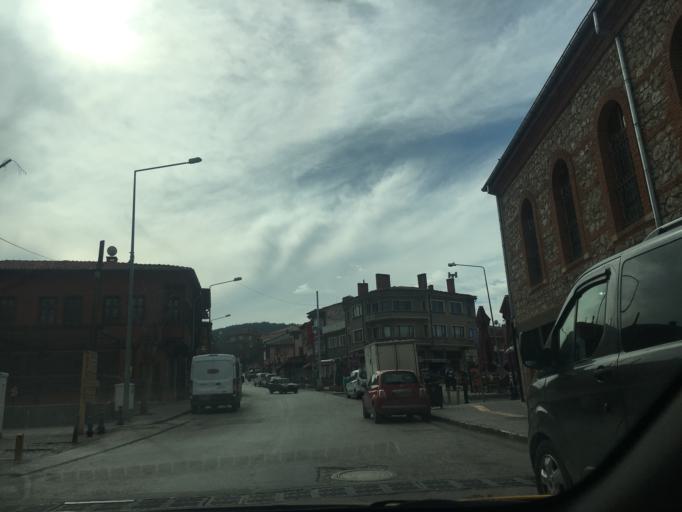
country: TR
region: Eskisehir
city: Eskisehir
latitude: 39.7648
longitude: 30.5240
